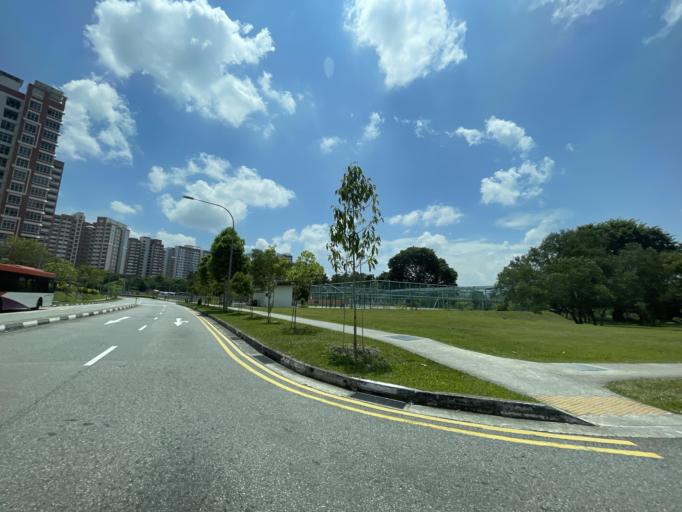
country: MY
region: Johor
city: Kampung Pasir Gudang Baru
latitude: 1.3828
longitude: 103.8798
